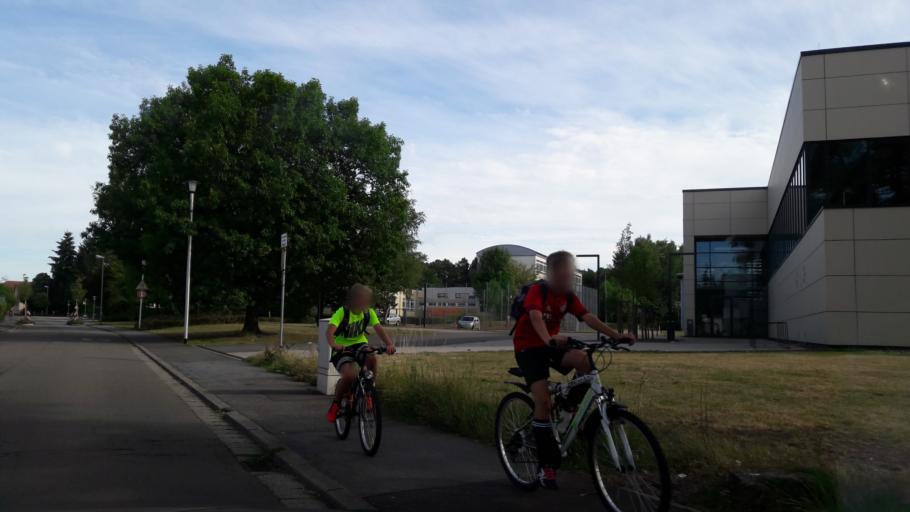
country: DE
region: Saarland
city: Homburg
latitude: 49.3345
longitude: 7.3235
